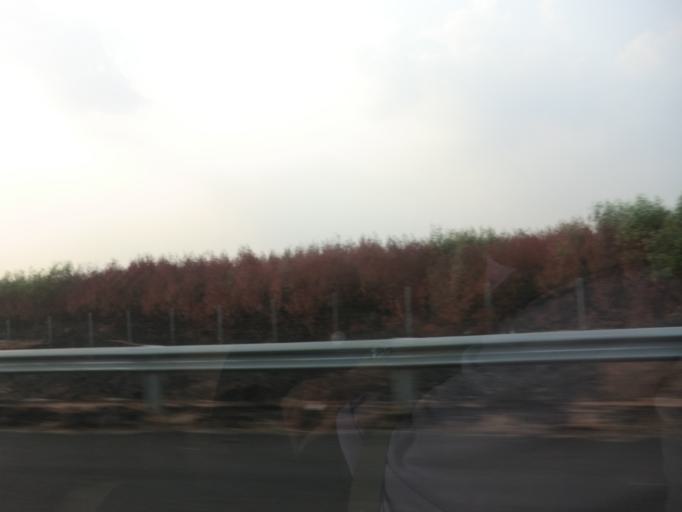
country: VN
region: Dong Nai
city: Long Thanh
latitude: 10.7841
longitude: 107.0214
